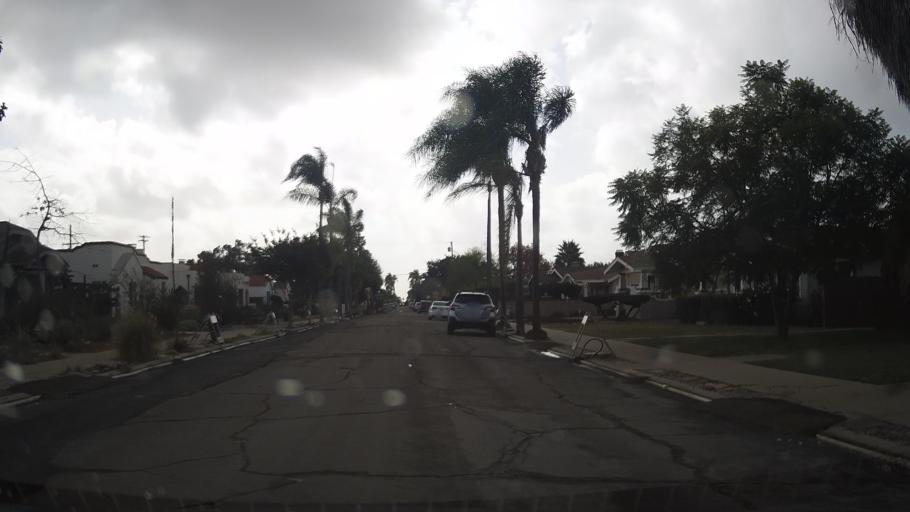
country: US
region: California
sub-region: San Diego County
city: San Diego
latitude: 32.7387
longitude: -117.1221
